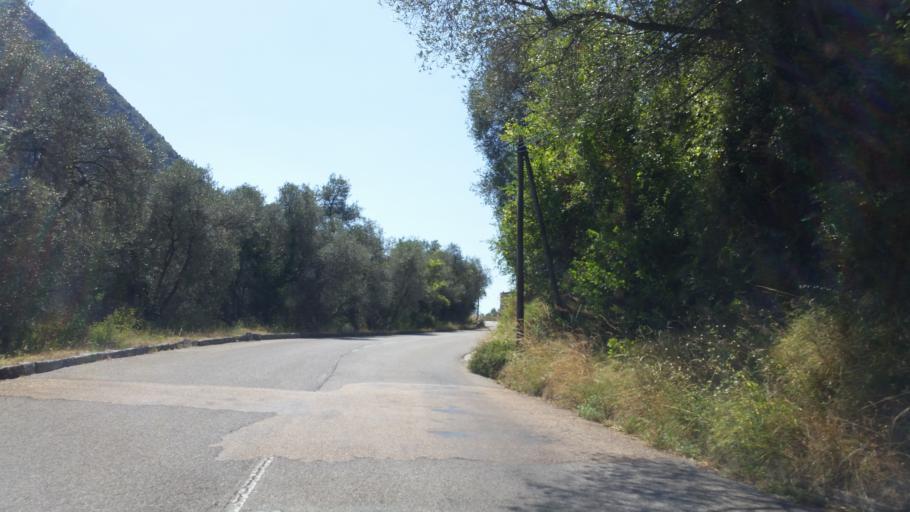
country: FR
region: Provence-Alpes-Cote d'Azur
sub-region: Departement des Alpes-Maritimes
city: Breil-sur-Roya
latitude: 43.9518
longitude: 7.5156
